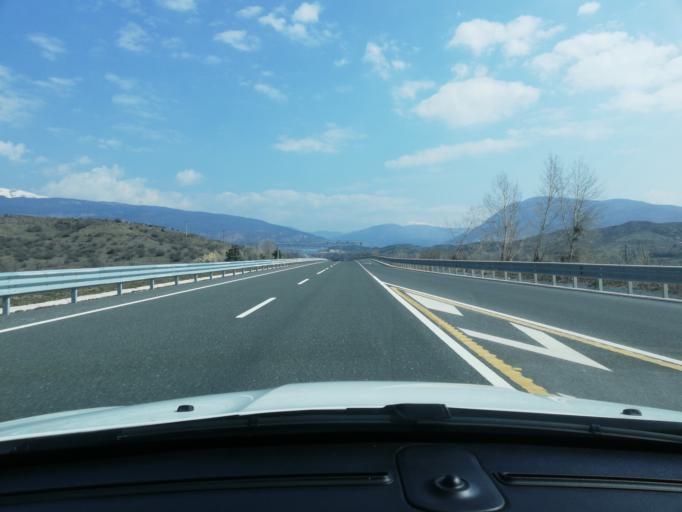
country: TR
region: Cankiri
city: Ilgaz
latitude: 40.9290
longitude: 33.6504
